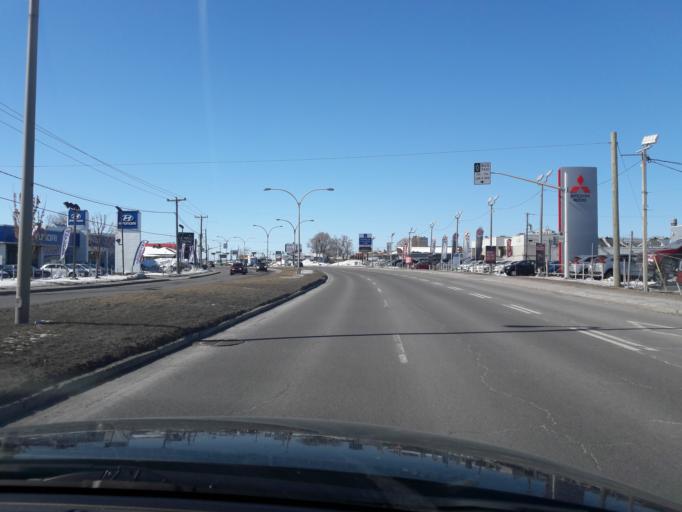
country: CA
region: Quebec
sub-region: Laval
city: Laval
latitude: 45.5598
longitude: -73.7699
